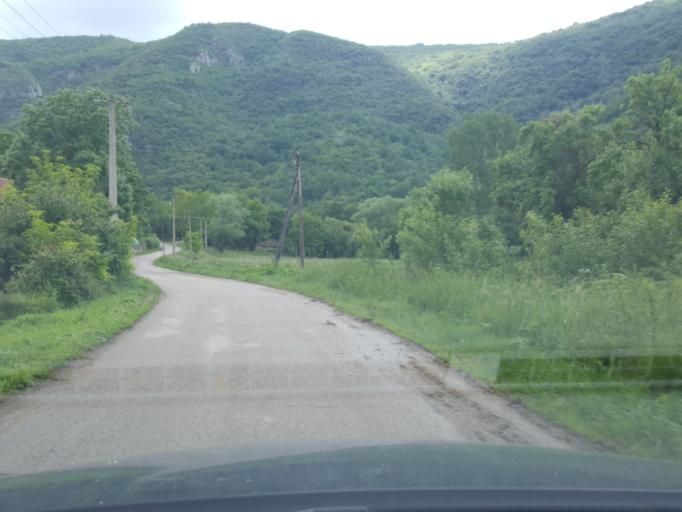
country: RS
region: Central Serbia
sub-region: Zajecarski Okrug
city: Soko Banja
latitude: 43.6335
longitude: 21.9894
